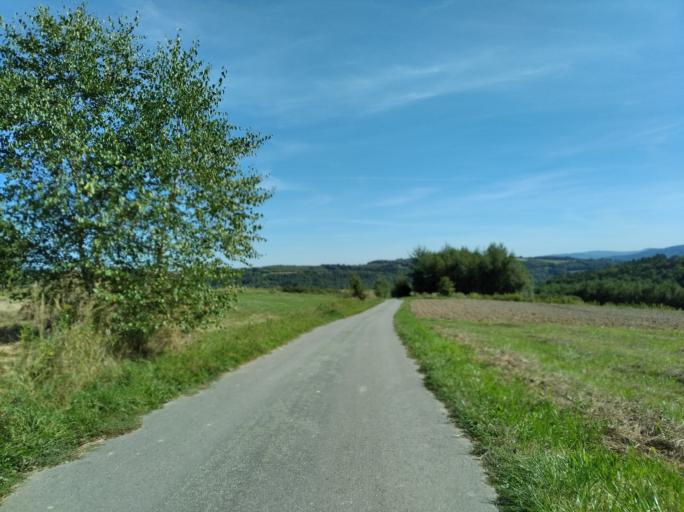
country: PL
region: Subcarpathian Voivodeship
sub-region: Powiat strzyzowski
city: Wisniowa
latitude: 49.8986
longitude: 21.6287
